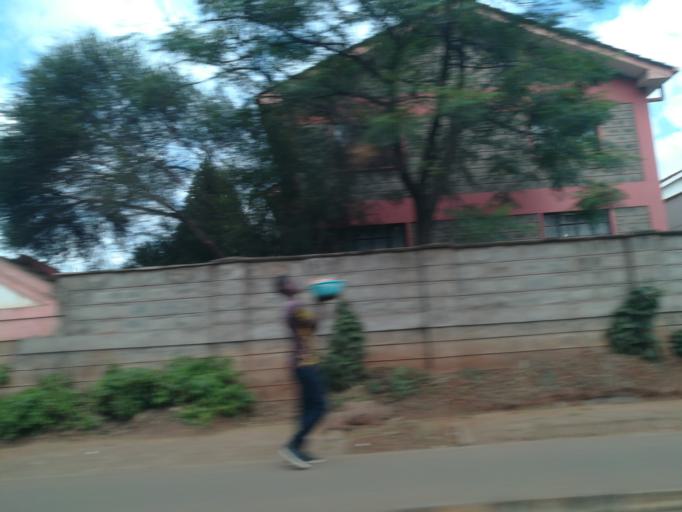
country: KE
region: Nairobi Area
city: Nairobi
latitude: -1.2830
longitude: 36.7862
